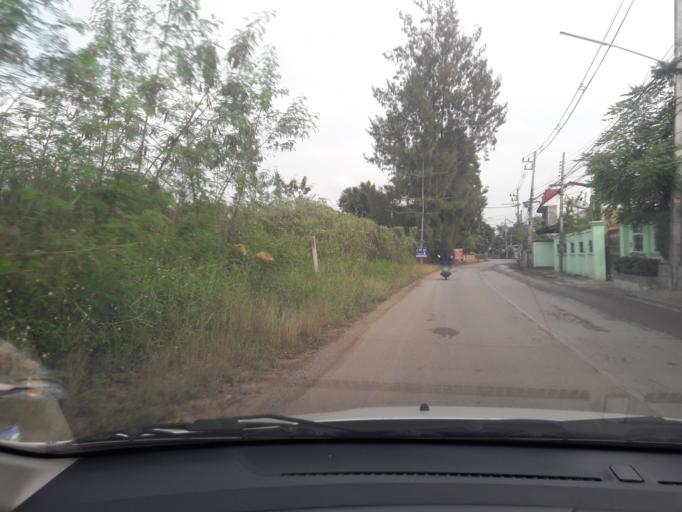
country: TH
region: Chiang Mai
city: Saraphi
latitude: 18.7143
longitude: 99.0472
